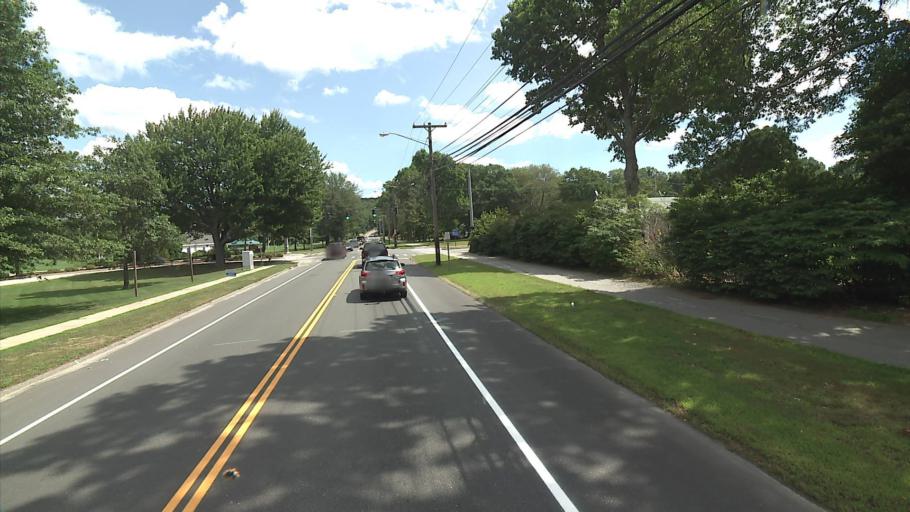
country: US
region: Connecticut
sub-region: New London County
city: Poquonock Bridge
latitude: 41.3466
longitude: -72.0249
